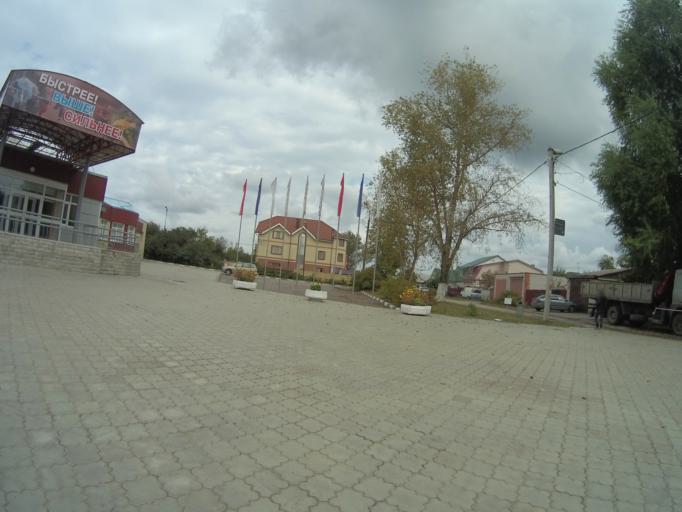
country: RU
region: Vladimir
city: Vladimir
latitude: 56.1146
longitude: 40.3608
